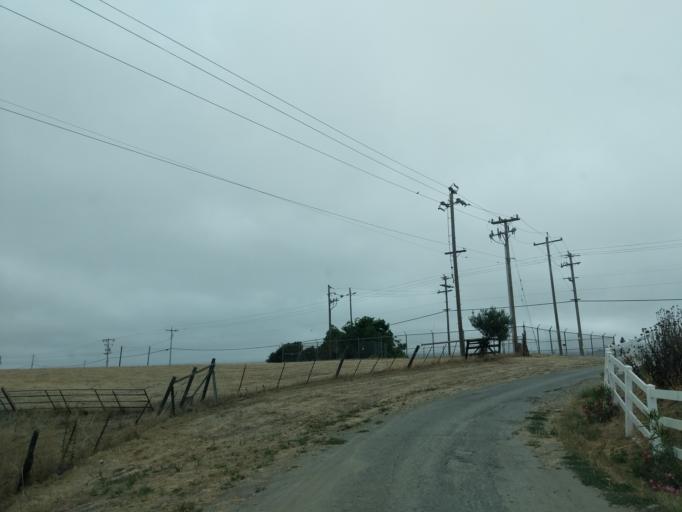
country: US
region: California
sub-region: San Benito County
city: Hollister
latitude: 36.8623
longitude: -121.3645
